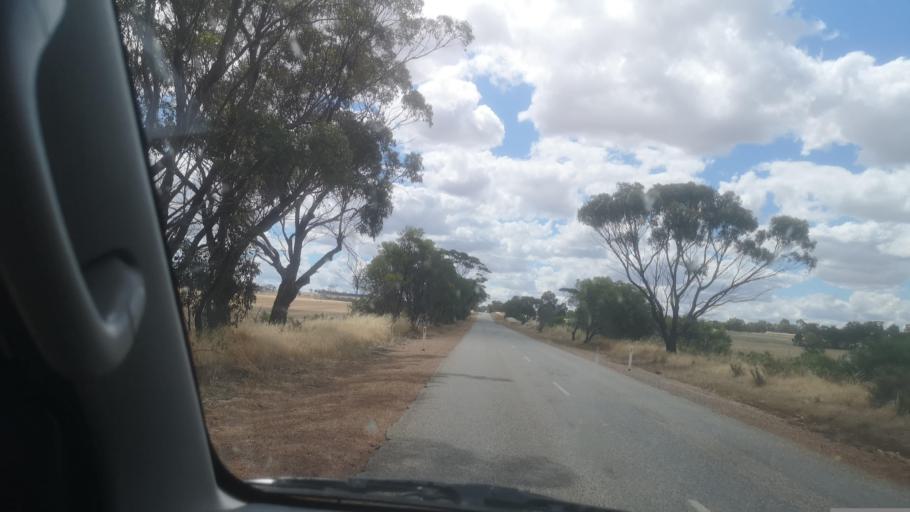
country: AU
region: Western Australia
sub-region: Beverley
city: Beverley
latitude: -31.9780
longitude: 117.0838
